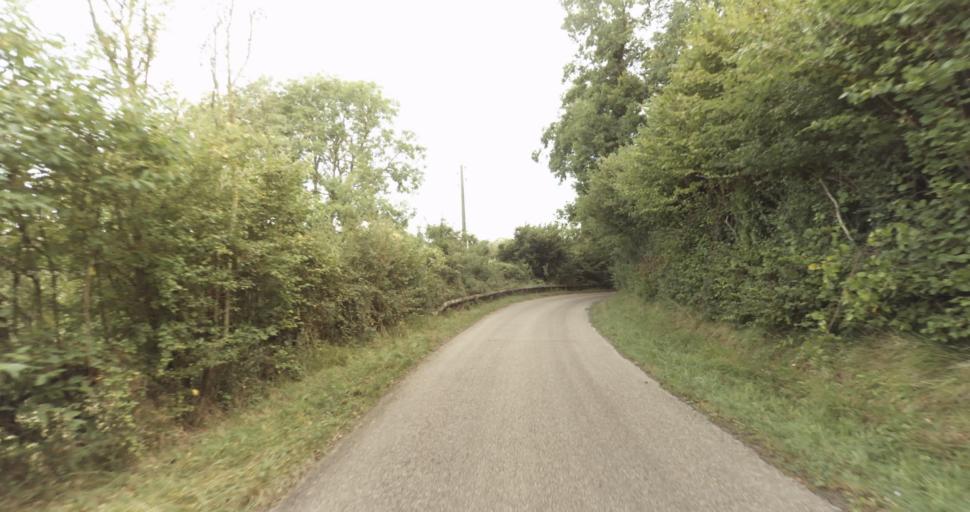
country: FR
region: Lower Normandy
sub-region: Departement de l'Orne
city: Vimoutiers
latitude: 48.8939
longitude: 0.2221
